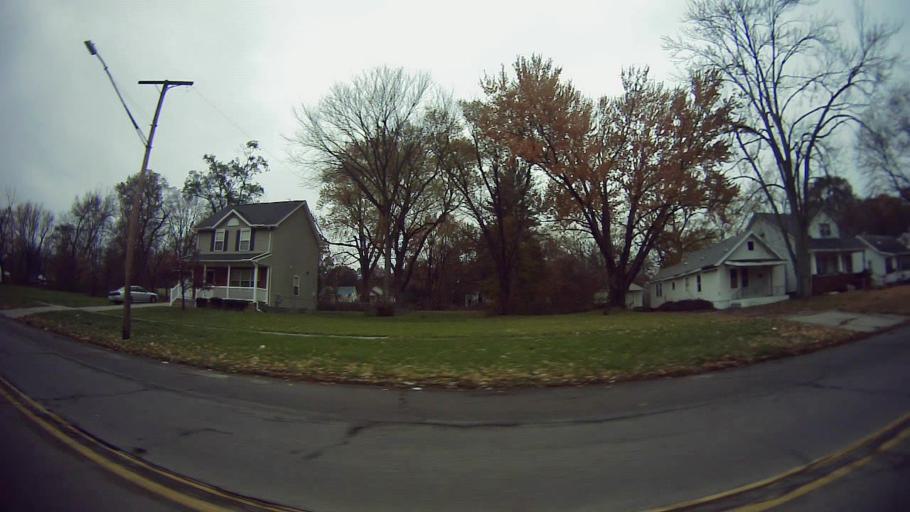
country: US
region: Michigan
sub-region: Wayne County
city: Redford
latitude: 42.3986
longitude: -83.2567
